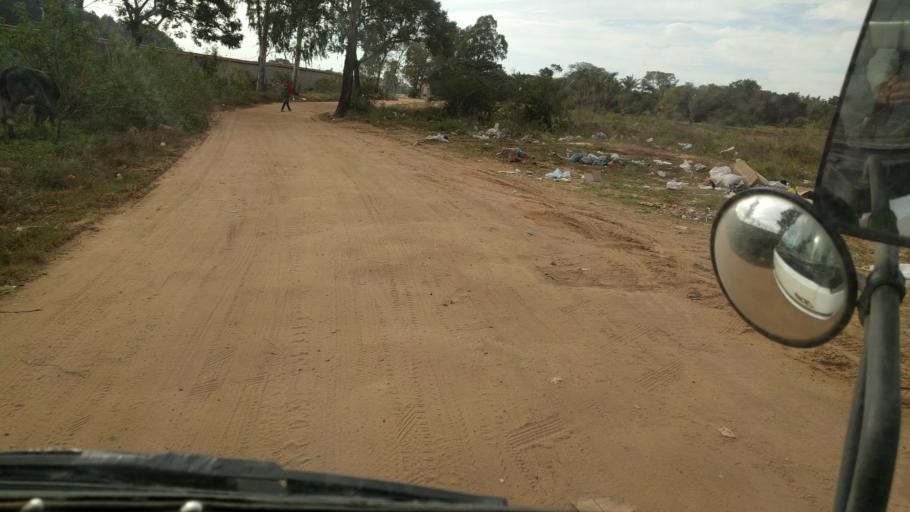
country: BO
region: Santa Cruz
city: Santa Cruz de la Sierra
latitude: -17.6812
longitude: -63.1426
